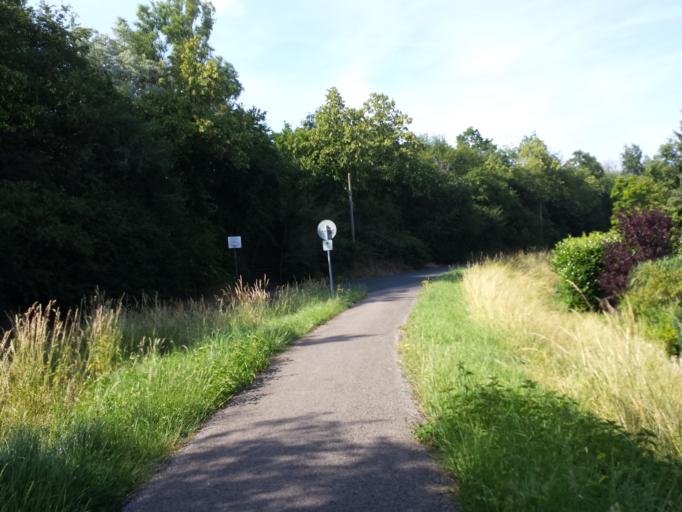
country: DE
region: Lower Saxony
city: Stuhr
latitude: 53.0954
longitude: 8.7442
